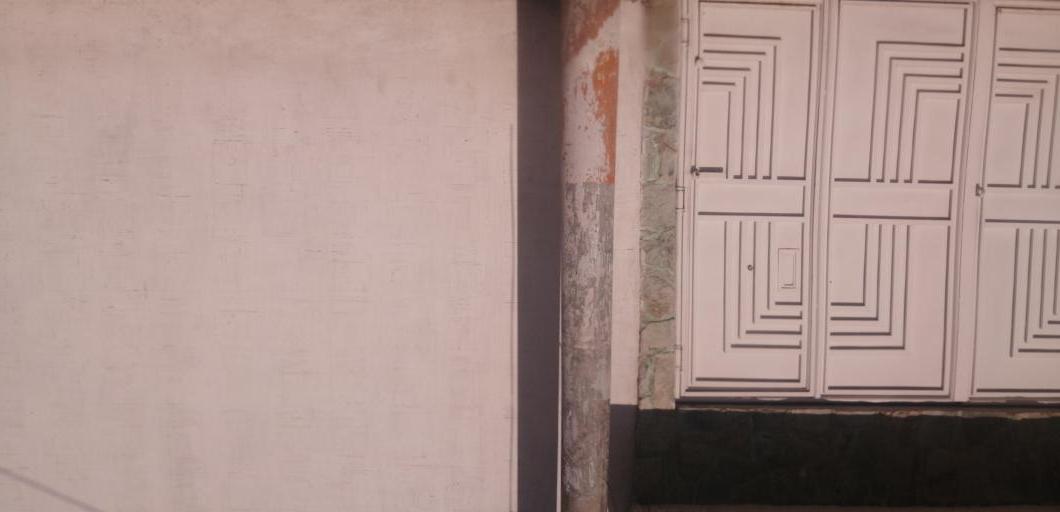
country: GT
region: Quetzaltenango
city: Quetzaltenango
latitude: 14.8432
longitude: -91.5320
